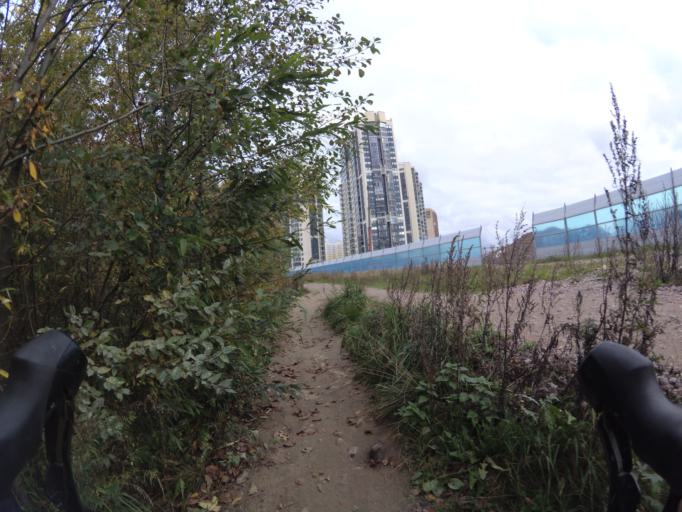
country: RU
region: Leningrad
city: Untolovo
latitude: 59.9930
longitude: 30.1909
